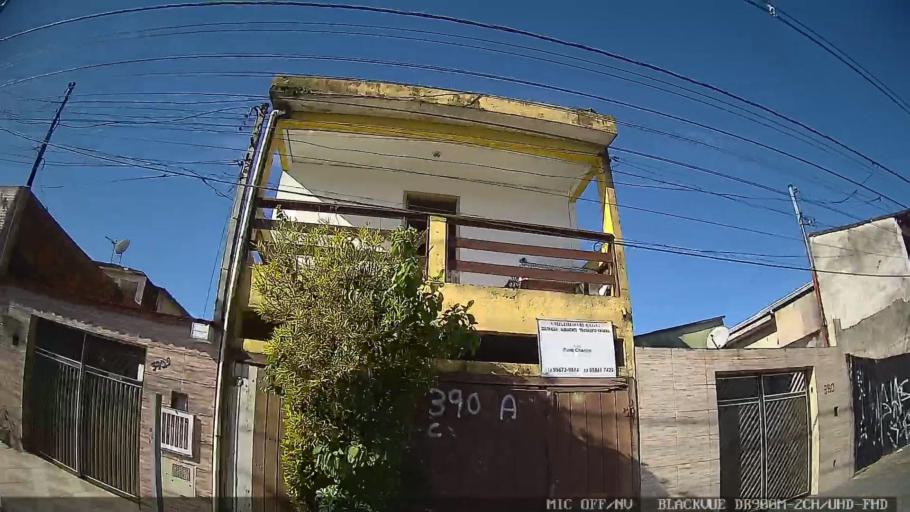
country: BR
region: Sao Paulo
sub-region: Santos
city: Santos
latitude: -23.9356
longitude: -46.2838
